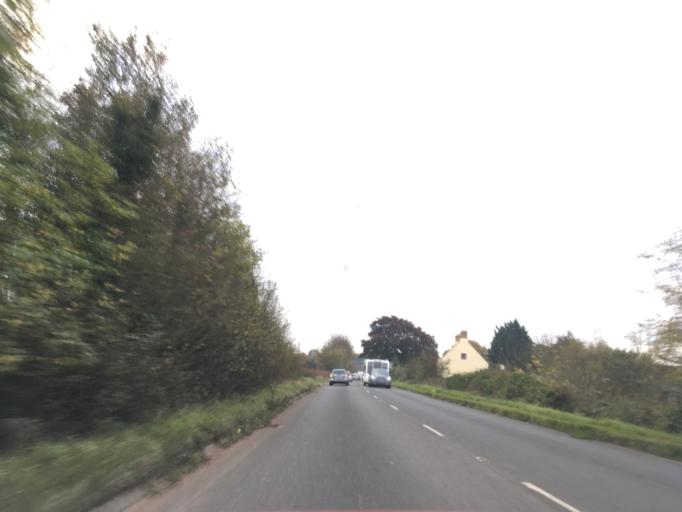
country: GB
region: England
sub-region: South Gloucestershire
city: Yate
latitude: 51.5244
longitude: -2.4352
